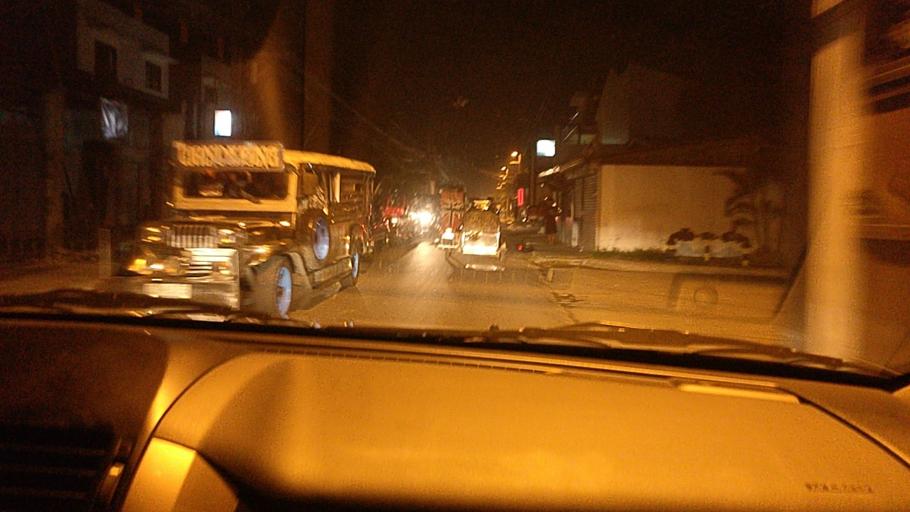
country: PH
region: Calabarzon
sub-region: Province of Cavite
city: Dasmarinas
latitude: 14.3761
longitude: 120.9299
